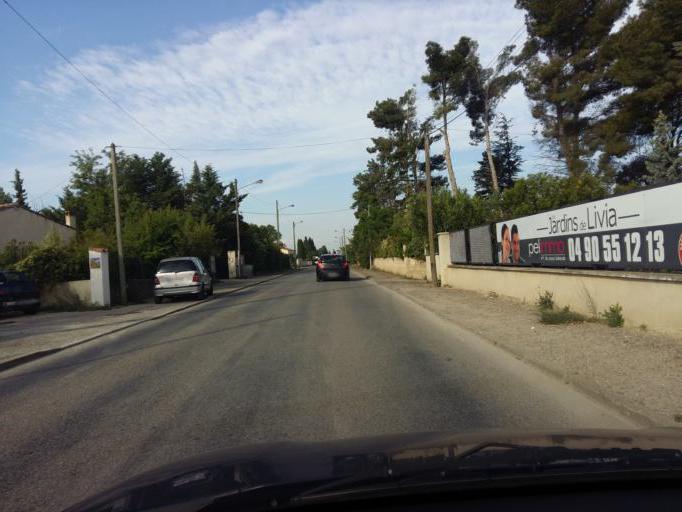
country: FR
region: Provence-Alpes-Cote d'Azur
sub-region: Departement des Bouches-du-Rhone
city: Pelissanne
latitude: 43.6277
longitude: 5.1537
